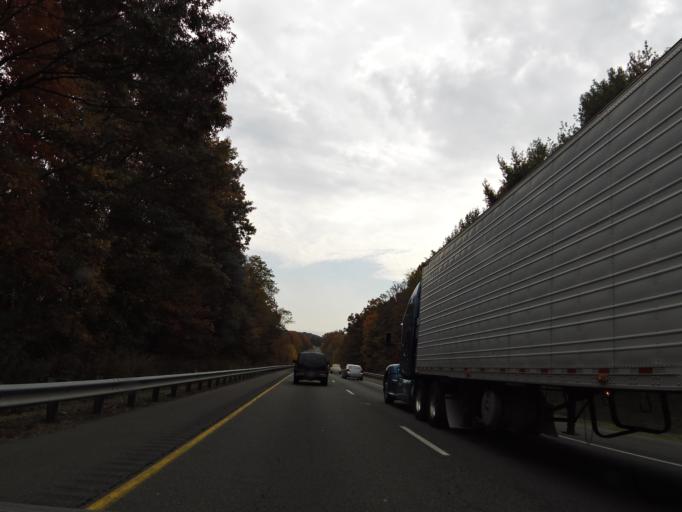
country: US
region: Virginia
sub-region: Carroll County
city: Woodlawn
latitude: 36.7965
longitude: -80.8426
